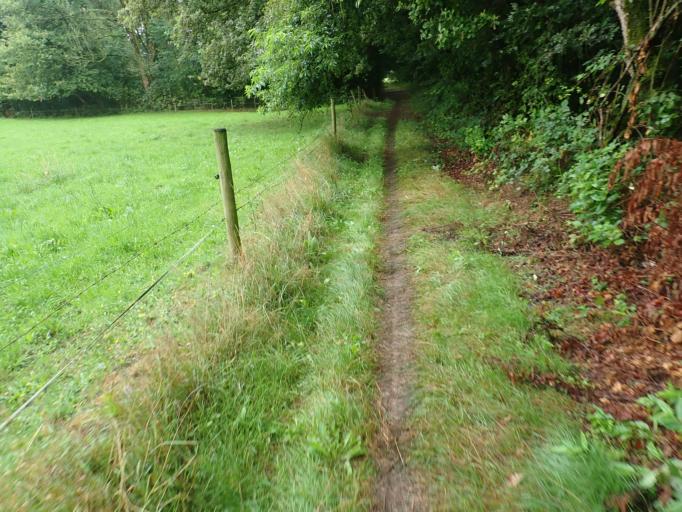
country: BE
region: Flanders
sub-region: Provincie Antwerpen
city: Zandhoven
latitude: 51.2452
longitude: 4.6626
